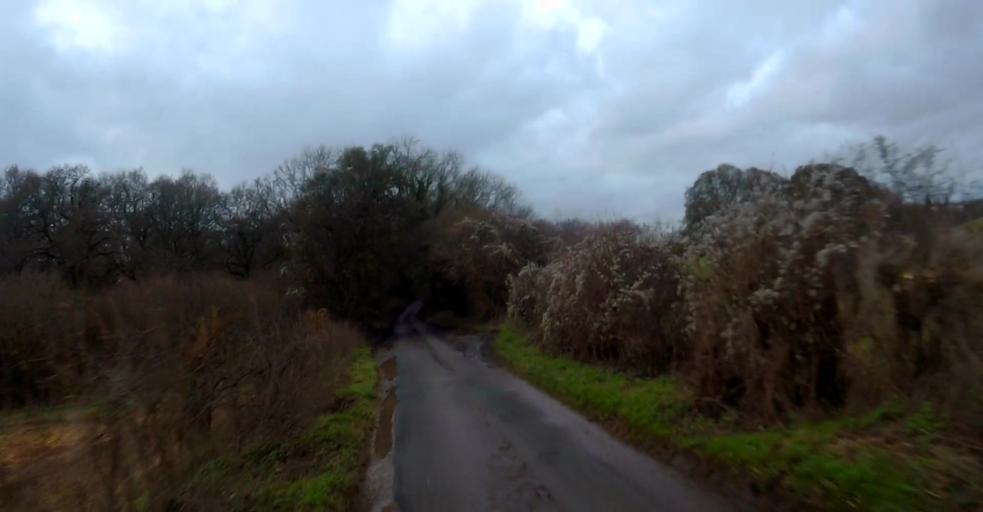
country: GB
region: England
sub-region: Hampshire
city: Overton
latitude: 51.2289
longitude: -1.2413
